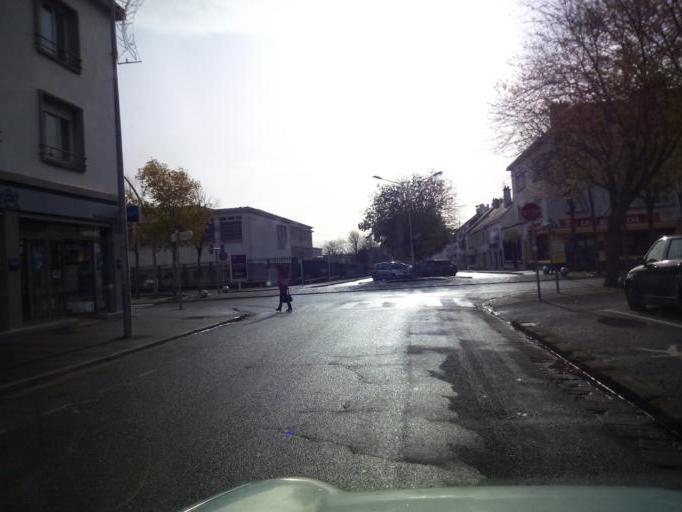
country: FR
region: Pays de la Loire
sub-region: Departement de la Loire-Atlantique
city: Saint-Nazaire
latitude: 47.2793
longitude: -2.2153
